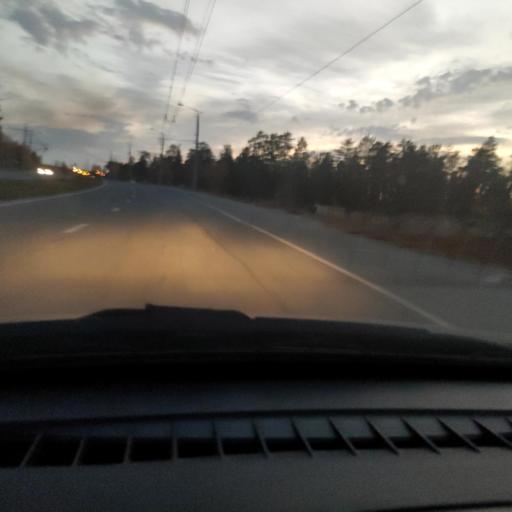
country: RU
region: Samara
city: Zhigulevsk
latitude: 53.5330
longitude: 49.5565
